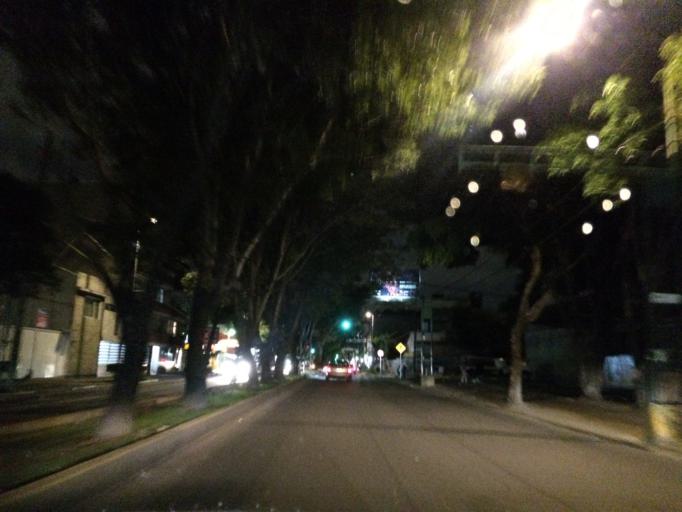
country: MX
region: Mexico City
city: Coyoacan
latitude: 19.3662
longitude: -99.1550
